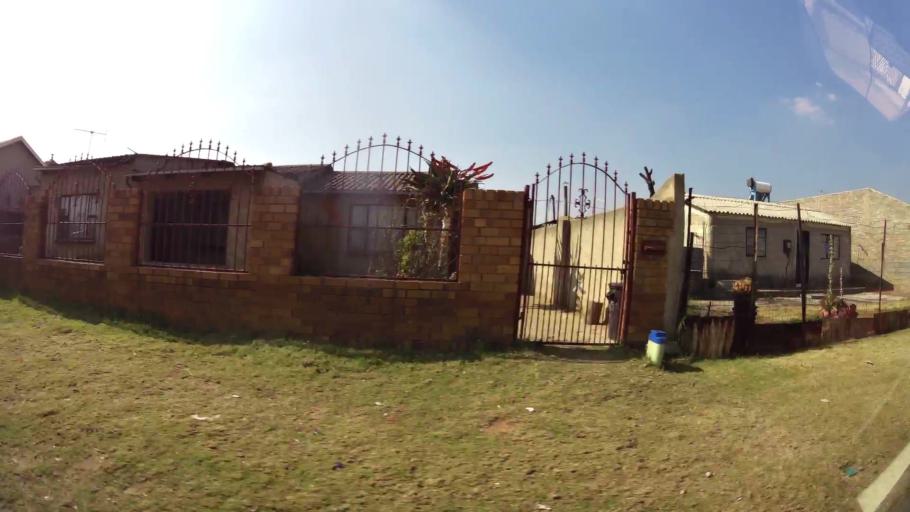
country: ZA
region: Gauteng
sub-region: Ekurhuleni Metropolitan Municipality
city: Brakpan
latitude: -26.1452
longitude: 28.4133
